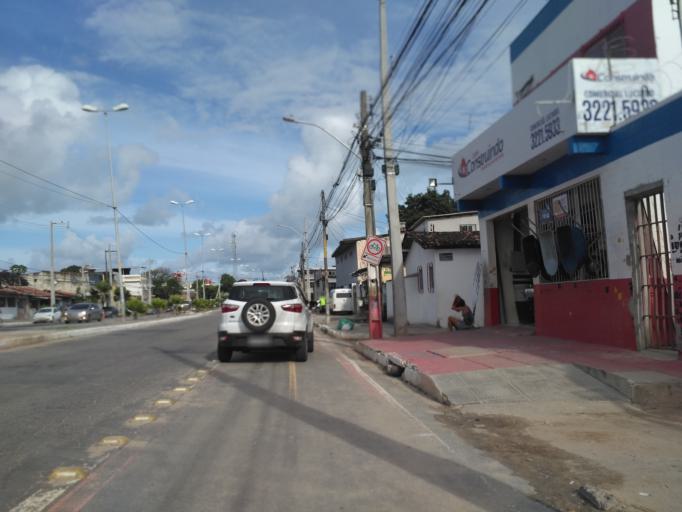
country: BR
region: Pernambuco
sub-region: Recife
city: Recife
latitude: -8.0417
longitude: -34.8776
